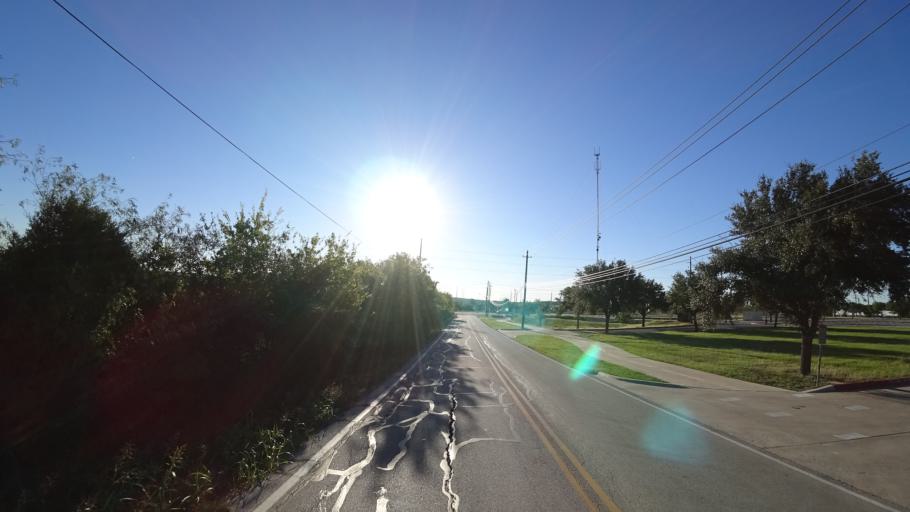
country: US
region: Texas
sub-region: Travis County
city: Manor
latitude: 30.3124
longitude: -97.6161
